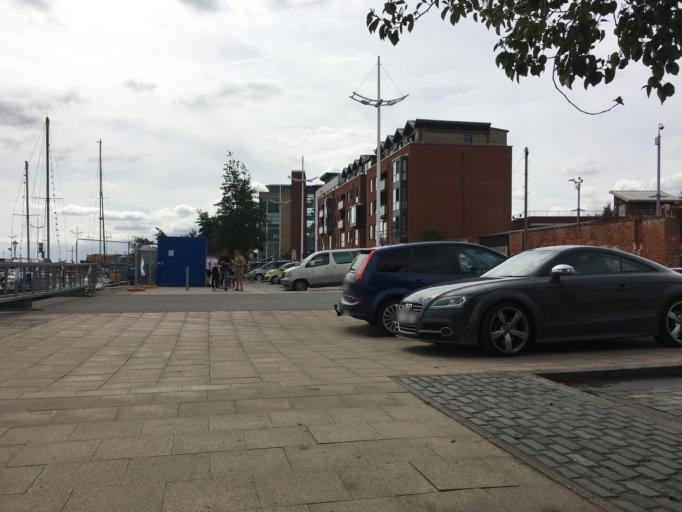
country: GB
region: England
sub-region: City of Kingston upon Hull
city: Hull
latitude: 53.7394
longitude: -0.3385
